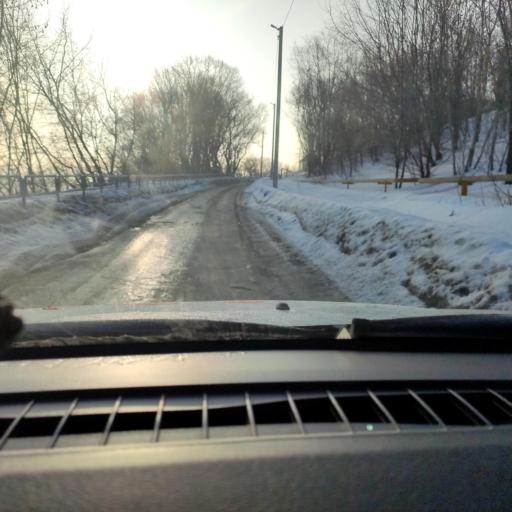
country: RU
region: Samara
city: Novokuybyshevsk
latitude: 53.1200
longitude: 49.9458
